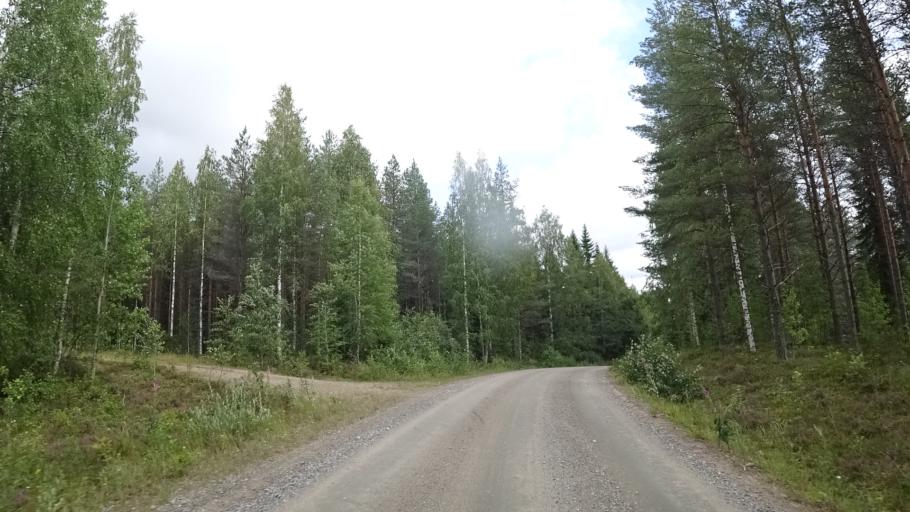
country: FI
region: North Karelia
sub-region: Joensuu
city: Ilomantsi
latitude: 62.9214
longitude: 31.3468
